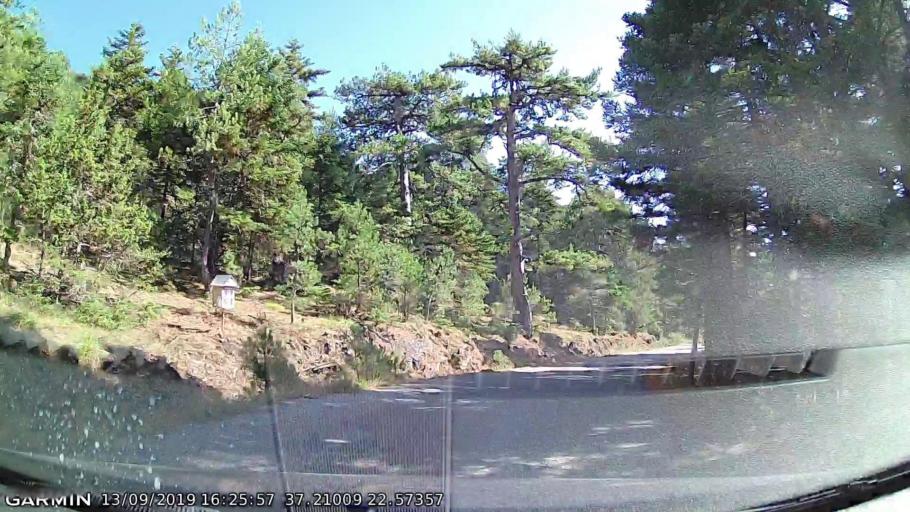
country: GR
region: Peloponnese
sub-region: Nomos Lakonias
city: Kariai
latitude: 37.2101
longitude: 22.5736
